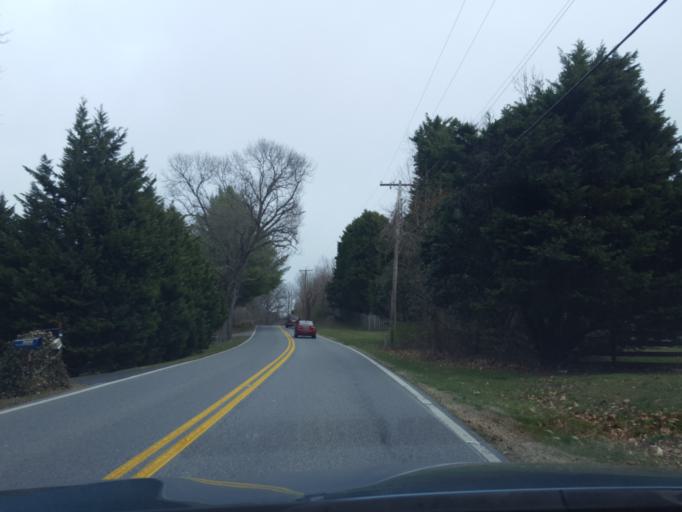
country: US
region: Maryland
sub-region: Calvert County
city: North Beach
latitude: 38.7118
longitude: -76.5660
